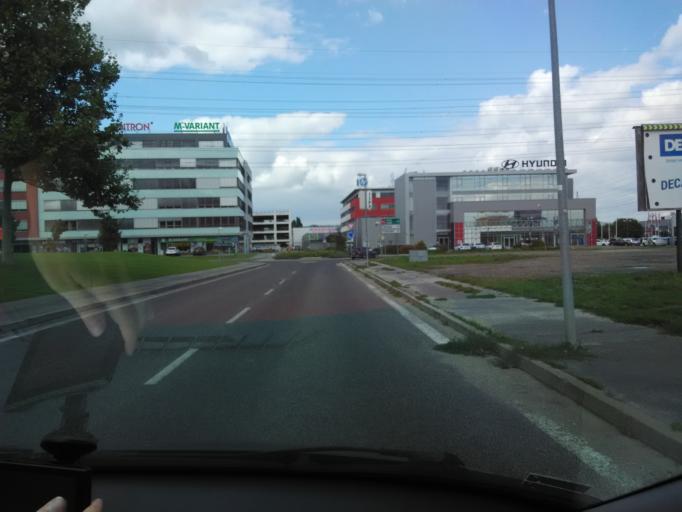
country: SK
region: Bratislavsky
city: Bratislava
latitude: 48.1636
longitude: 17.1787
